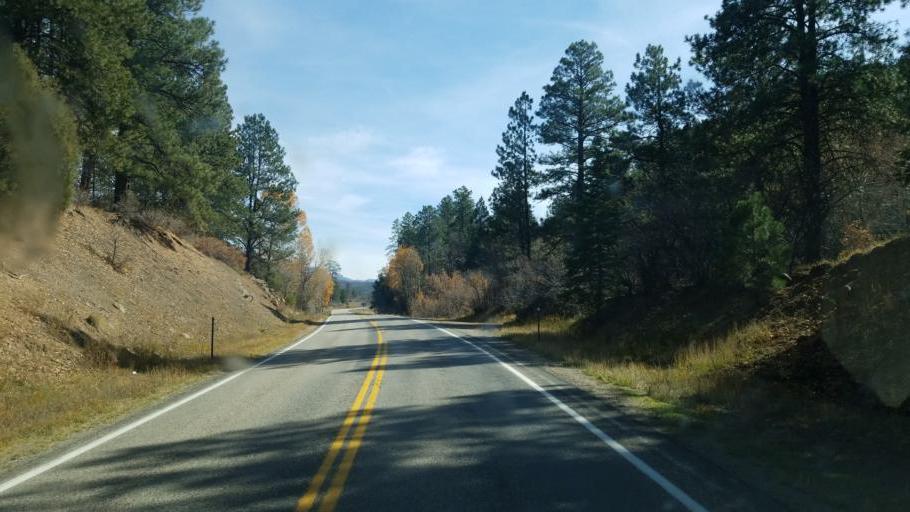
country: US
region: New Mexico
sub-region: Rio Arriba County
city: Dulce
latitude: 37.0750
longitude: -106.8460
